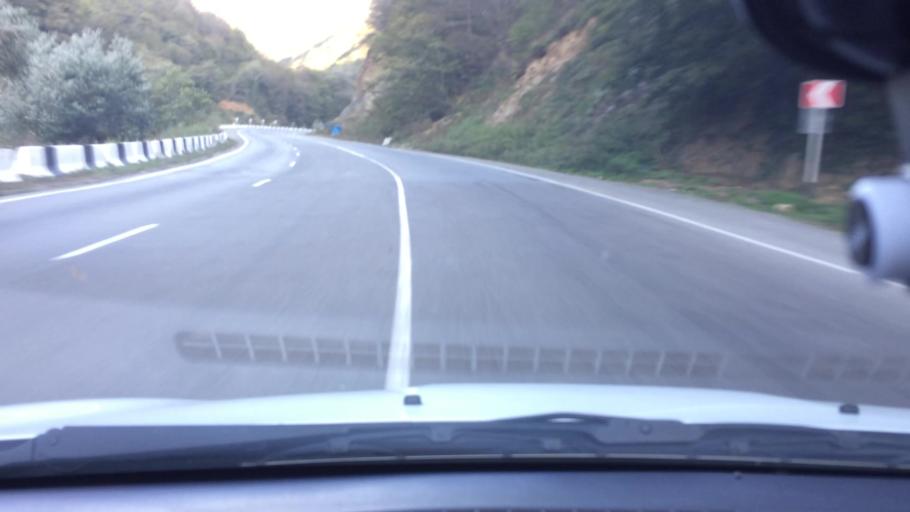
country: GE
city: Surami
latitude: 42.0886
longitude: 43.4657
